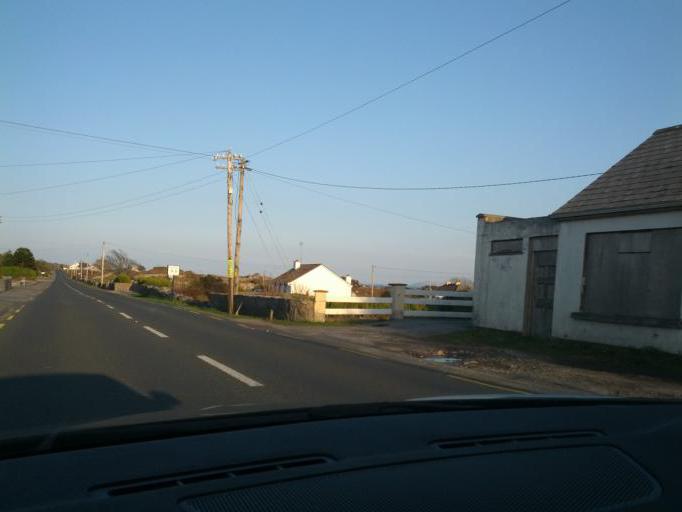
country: IE
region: Connaught
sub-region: County Galway
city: Oughterard
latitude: 53.2441
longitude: -9.3341
